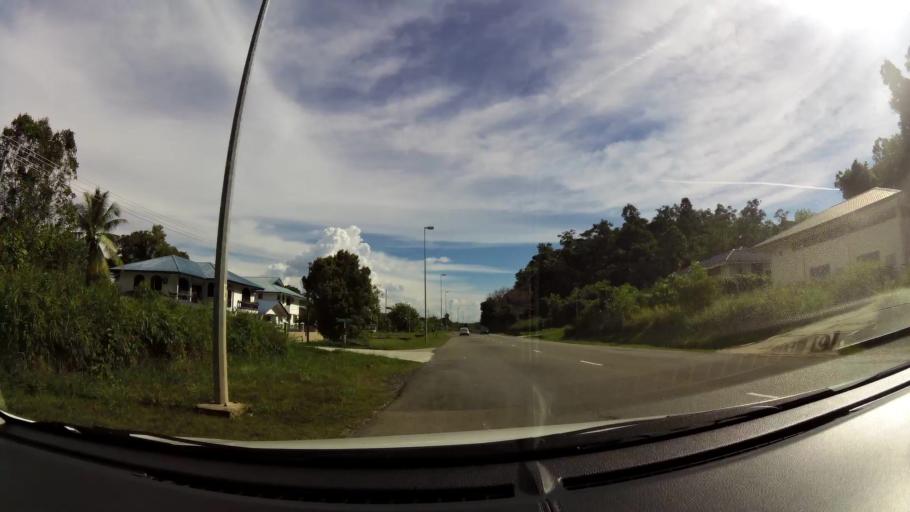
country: BN
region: Brunei and Muara
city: Bandar Seri Begawan
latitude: 5.0210
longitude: 115.0394
